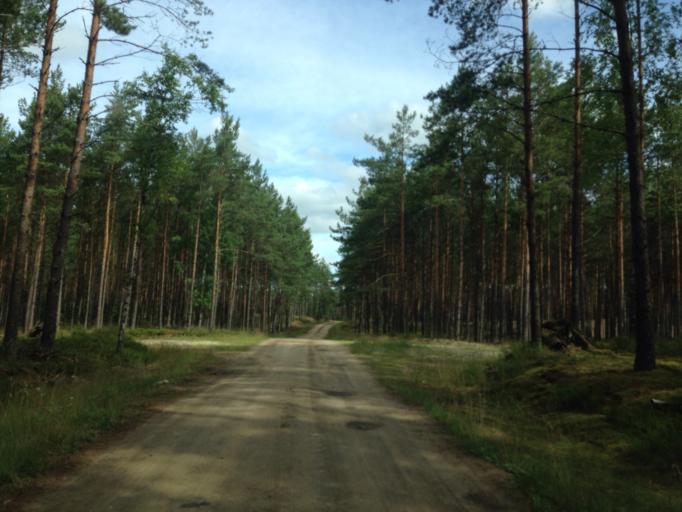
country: PL
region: Pomeranian Voivodeship
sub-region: Powiat bytowski
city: Studzienice
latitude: 54.0653
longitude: 17.6555
